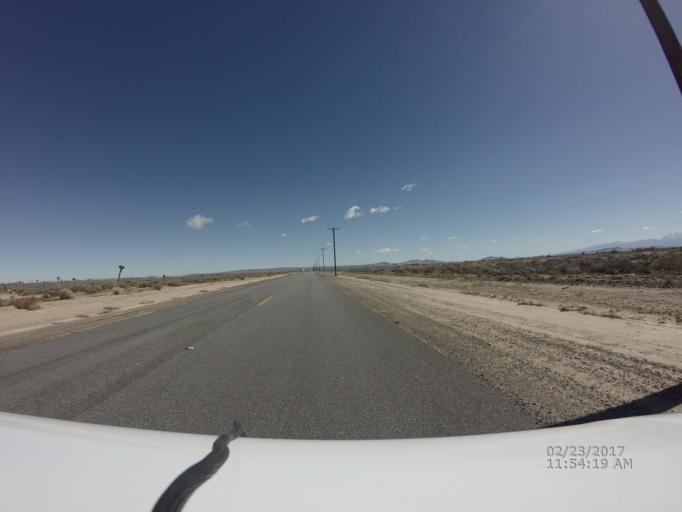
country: US
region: California
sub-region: Los Angeles County
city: Lancaster
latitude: 34.7344
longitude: -117.9819
